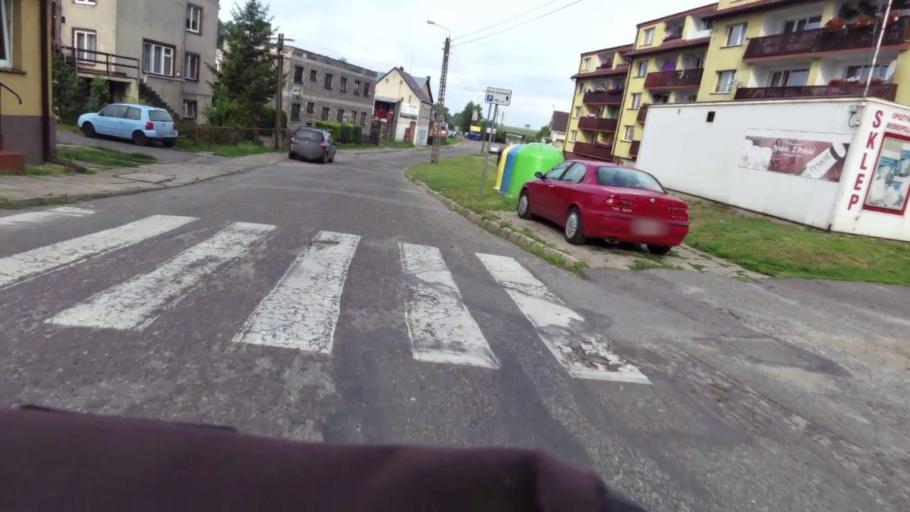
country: PL
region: West Pomeranian Voivodeship
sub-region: Powiat kamienski
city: Kamien Pomorski
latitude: 53.9681
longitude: 14.7672
